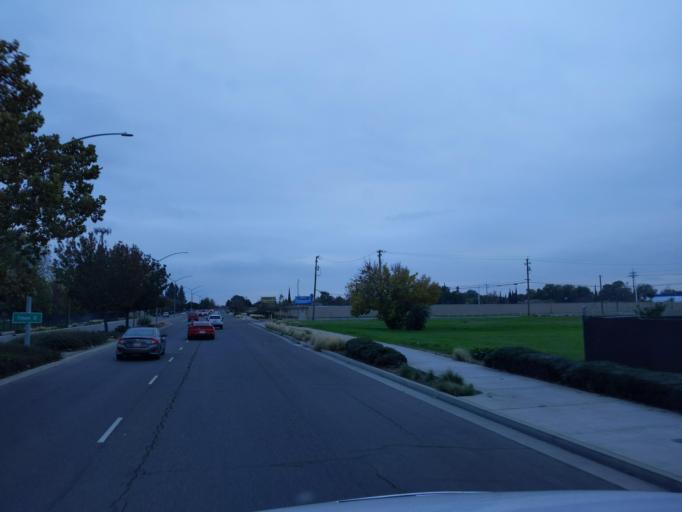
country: US
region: California
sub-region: San Joaquin County
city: Kennedy
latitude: 37.9371
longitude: -121.2692
